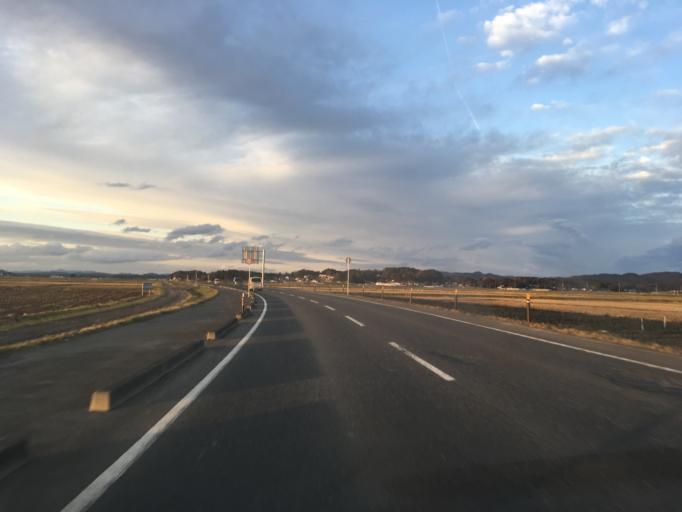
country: JP
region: Miyagi
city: Wakuya
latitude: 38.6793
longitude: 141.2610
